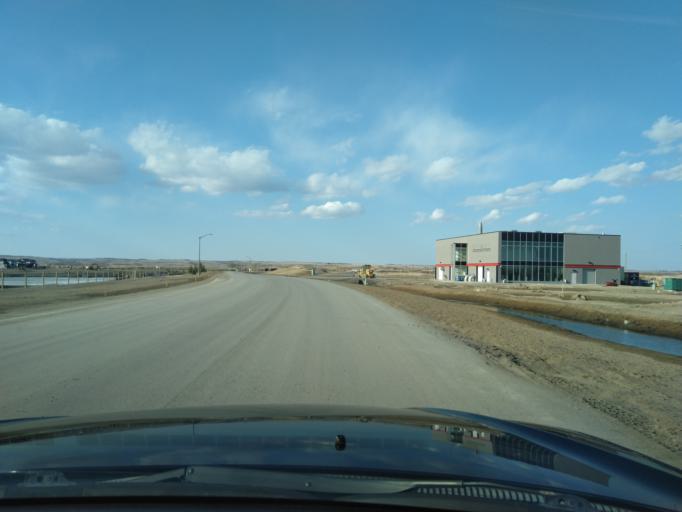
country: CA
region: Alberta
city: Cochrane
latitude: 51.1154
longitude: -114.3898
